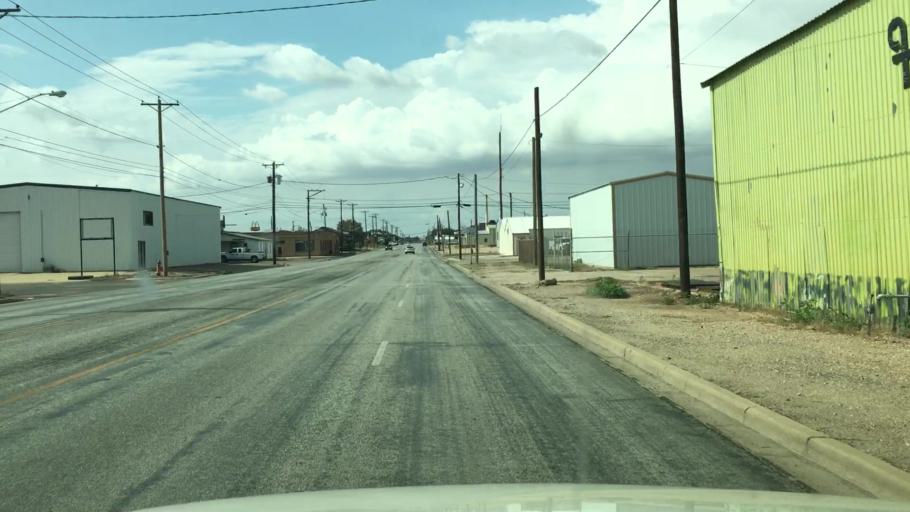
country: US
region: Texas
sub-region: Dawson County
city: Lamesa
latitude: 32.7324
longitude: -101.9488
